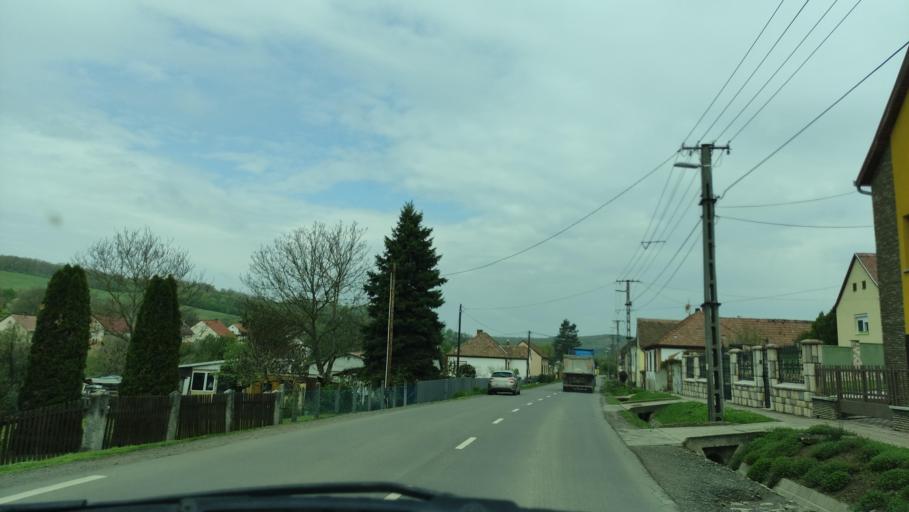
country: HU
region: Baranya
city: Komlo
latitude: 46.2126
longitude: 18.2437
